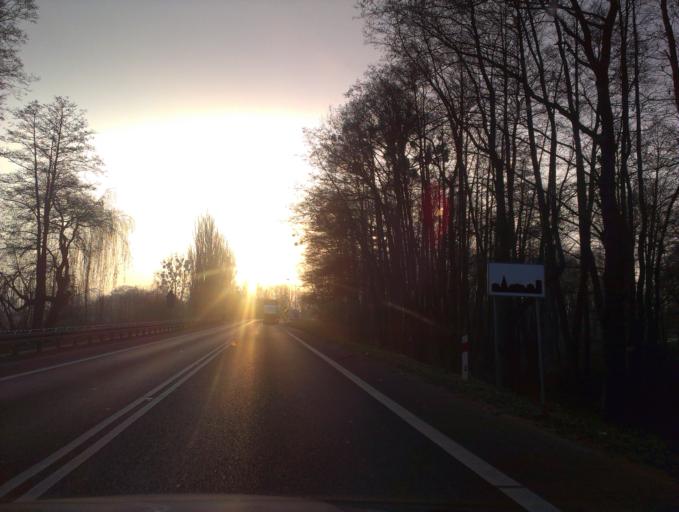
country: PL
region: Greater Poland Voivodeship
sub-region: Powiat obornicki
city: Rogozno
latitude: 52.7631
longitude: 16.9636
